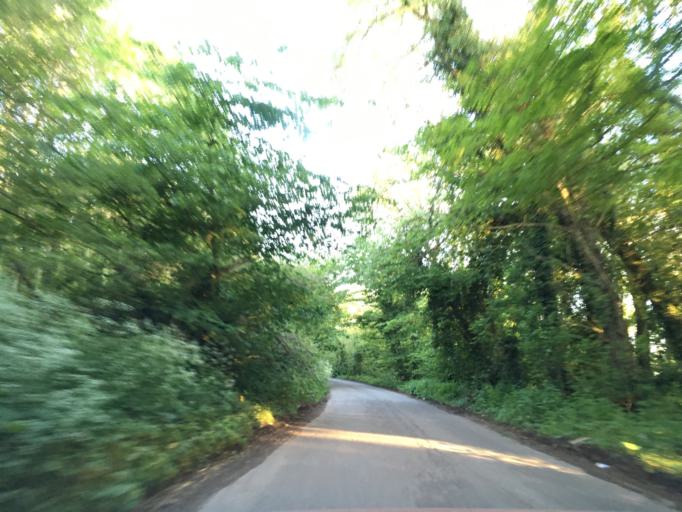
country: GB
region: Wales
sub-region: Newport
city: Llanwern
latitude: 51.5851
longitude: -2.9053
